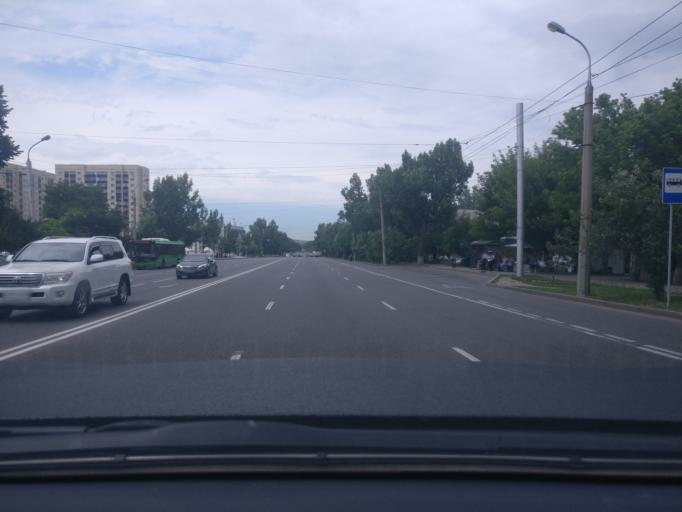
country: KZ
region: Almaty Qalasy
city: Almaty
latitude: 43.2388
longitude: 76.8595
